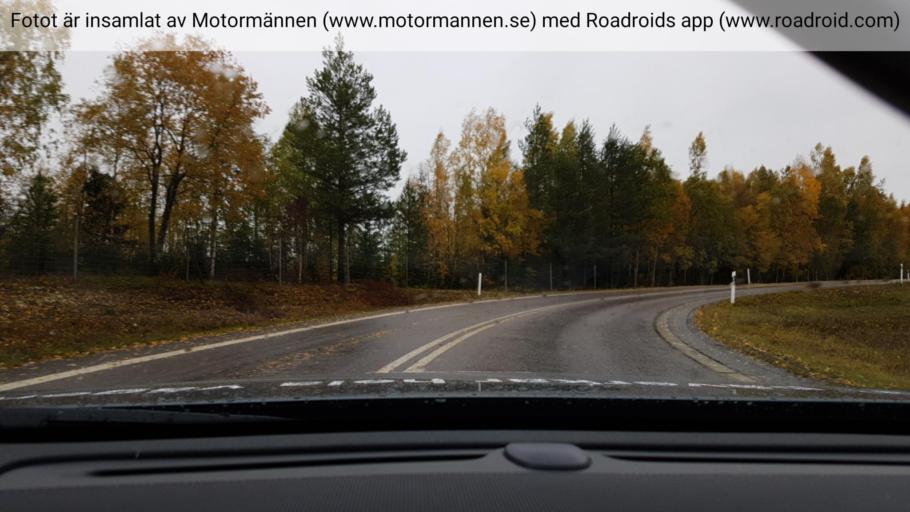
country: SE
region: Norrbotten
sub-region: Lulea Kommun
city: Gammelstad
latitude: 65.5835
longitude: 21.9961
